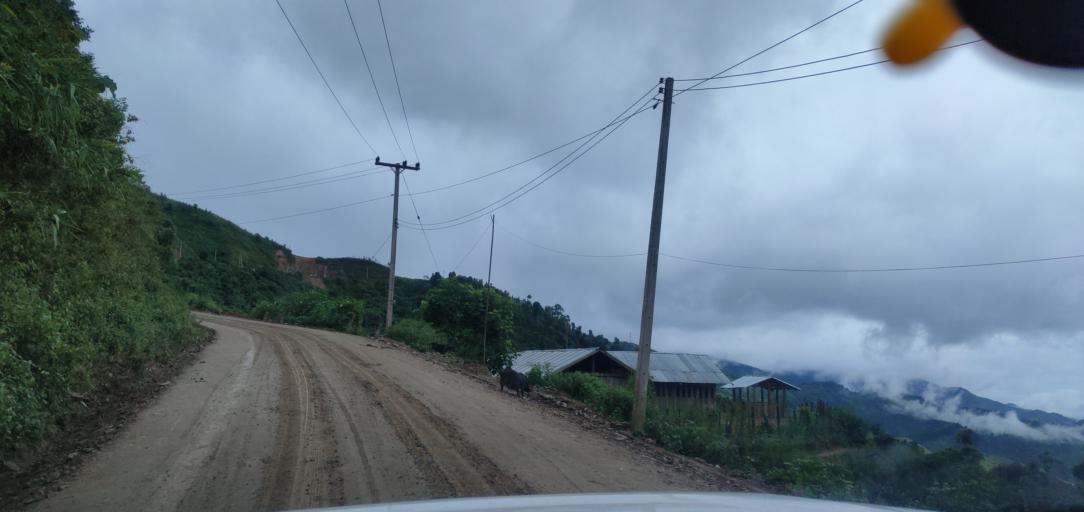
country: LA
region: Phongsali
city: Phongsali
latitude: 21.4280
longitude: 102.1676
